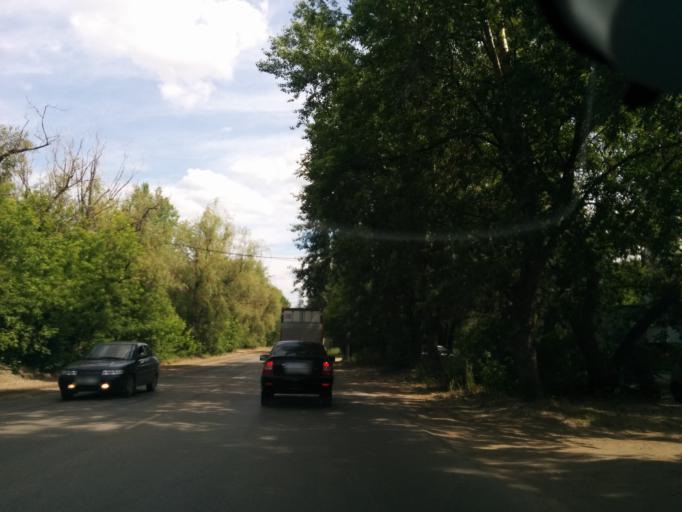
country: RU
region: Perm
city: Overyata
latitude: 58.0112
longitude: 55.9517
